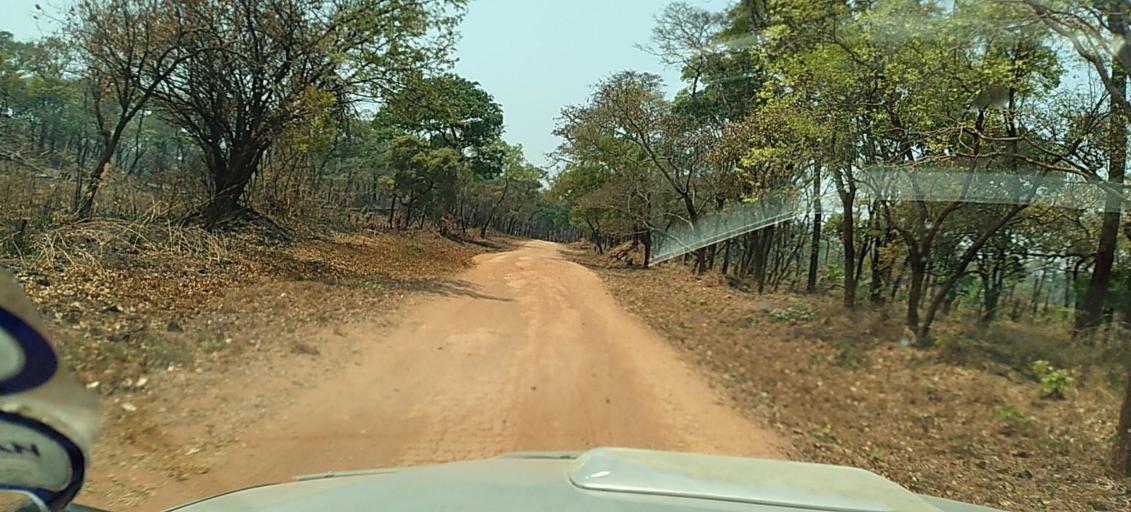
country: ZM
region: North-Western
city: Kasempa
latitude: -13.5446
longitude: 26.0454
